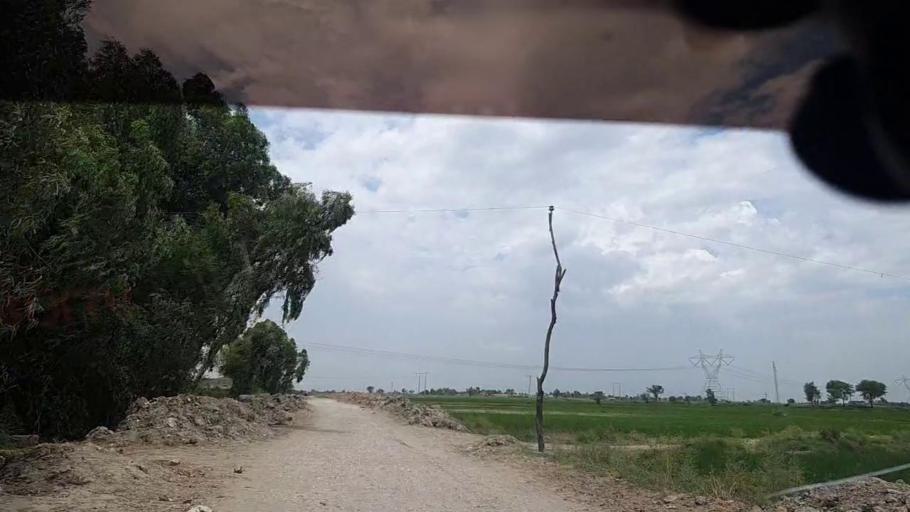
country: PK
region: Sindh
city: Ghauspur
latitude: 28.1081
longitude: 68.9861
